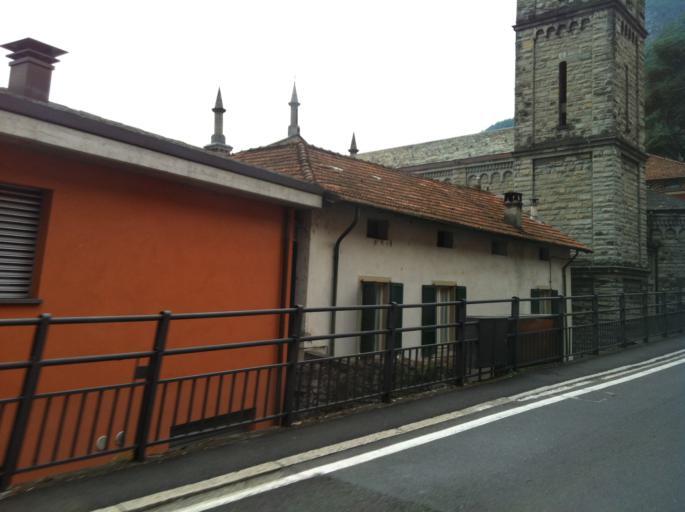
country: IT
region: Lombardy
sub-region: Provincia di Como
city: Argegno
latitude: 45.9457
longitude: 9.1287
